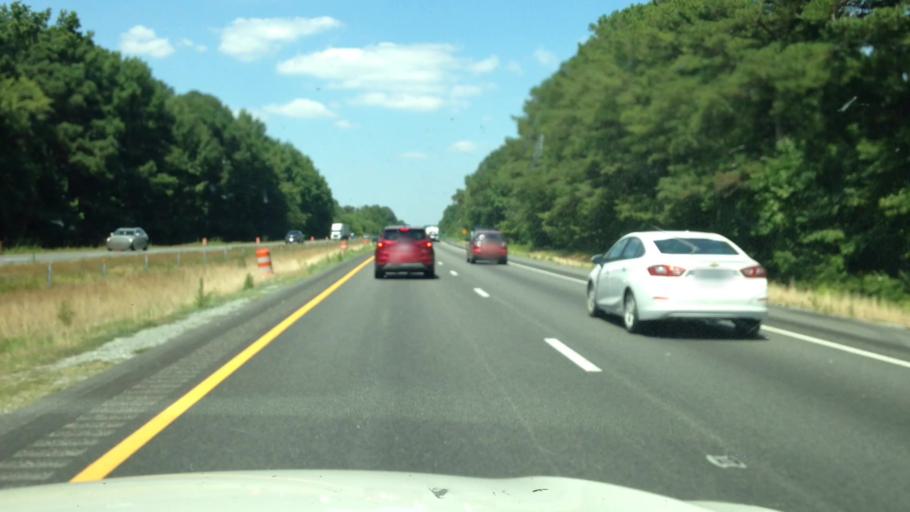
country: US
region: North Carolina
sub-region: Johnston County
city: Smithfield
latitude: 35.4739
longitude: -78.3729
